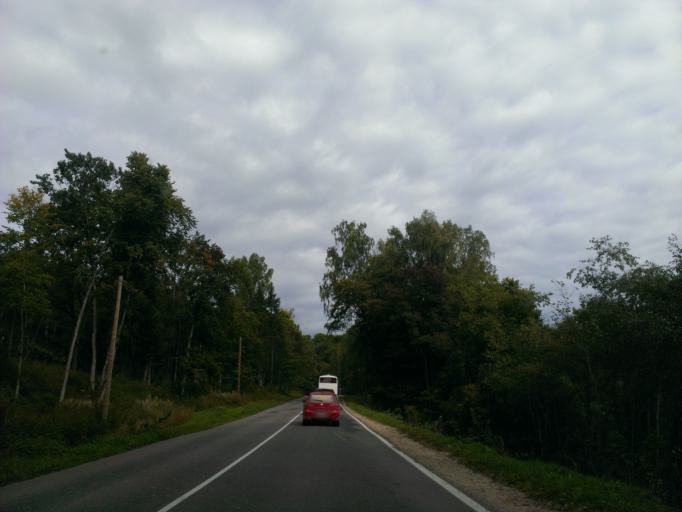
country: LV
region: Sigulda
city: Sigulda
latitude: 57.1776
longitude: 24.8475
